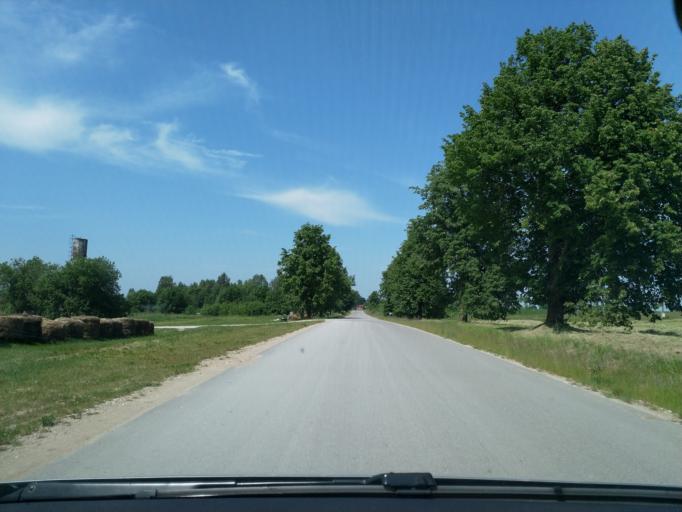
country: LV
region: Kuldigas Rajons
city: Kuldiga
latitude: 56.9555
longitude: 22.0144
